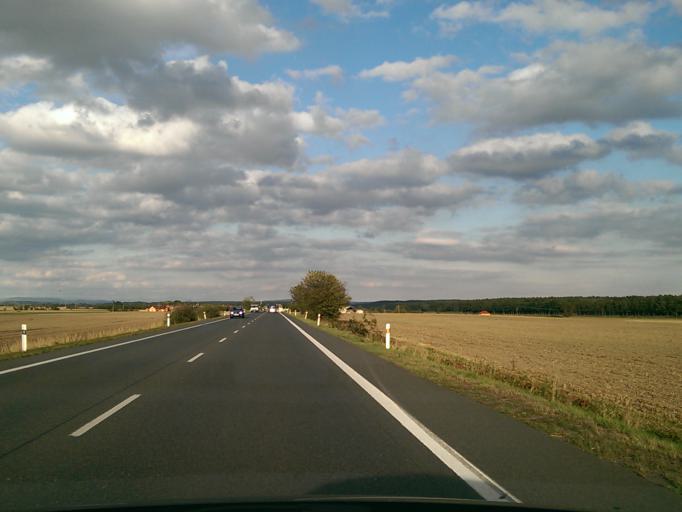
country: CZ
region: Central Bohemia
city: Dobrovice
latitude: 50.4207
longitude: 15.0128
